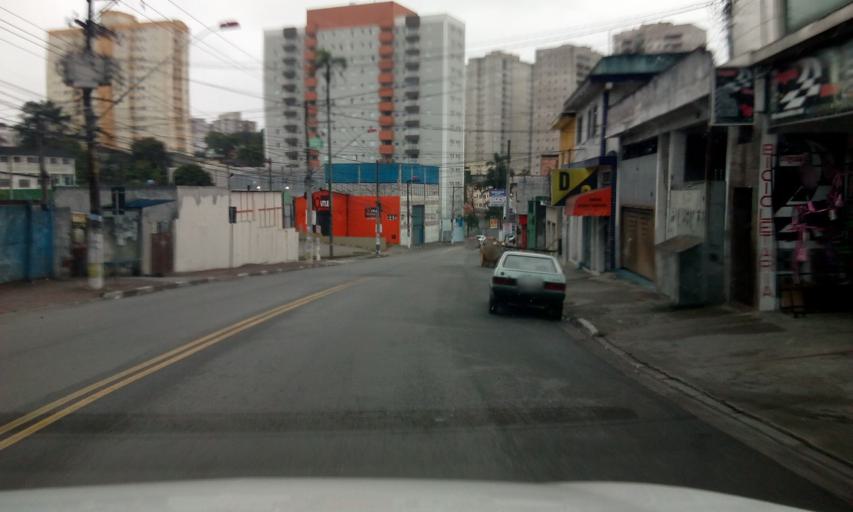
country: BR
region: Sao Paulo
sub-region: Diadema
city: Diadema
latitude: -23.6965
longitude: -46.6287
